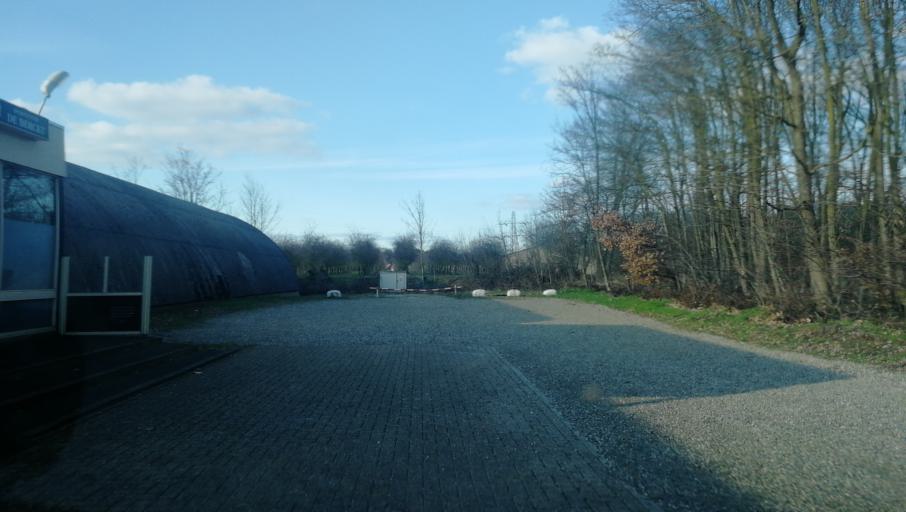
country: NL
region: Limburg
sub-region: Gemeente Venlo
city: Tegelen
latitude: 51.3447
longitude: 6.1004
